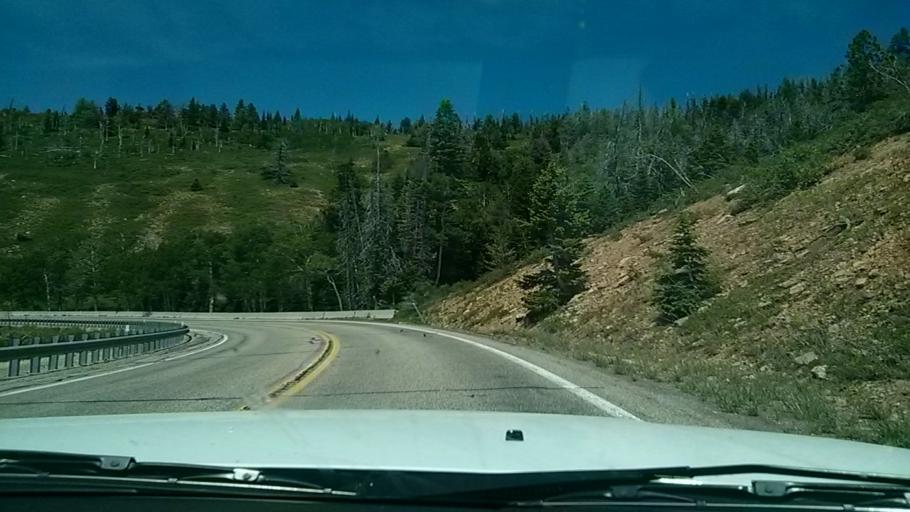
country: US
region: Utah
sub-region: Iron County
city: Cedar City
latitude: 37.5819
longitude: -112.8757
